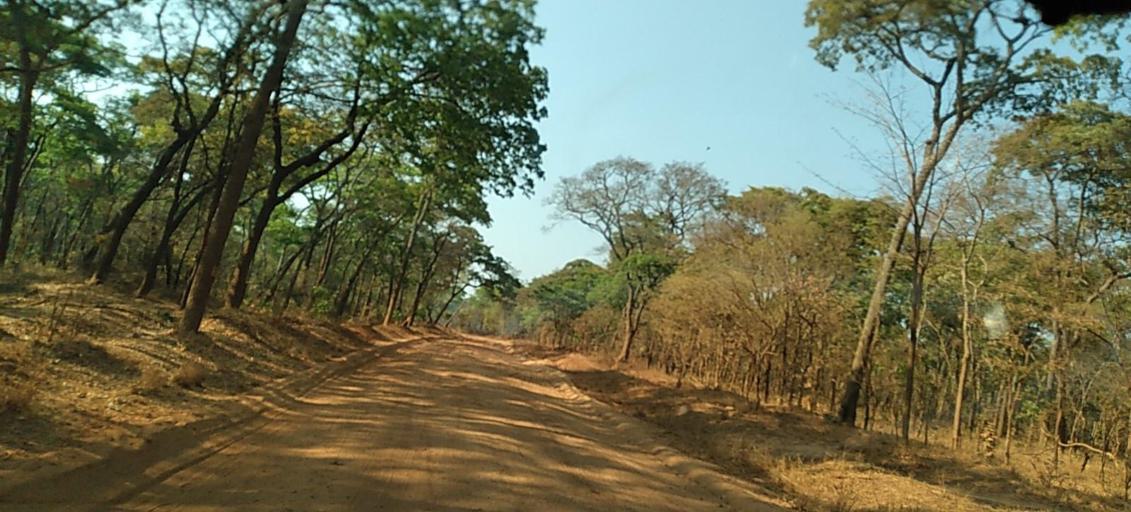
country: ZM
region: North-Western
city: Kasempa
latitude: -13.6149
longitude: 25.9792
